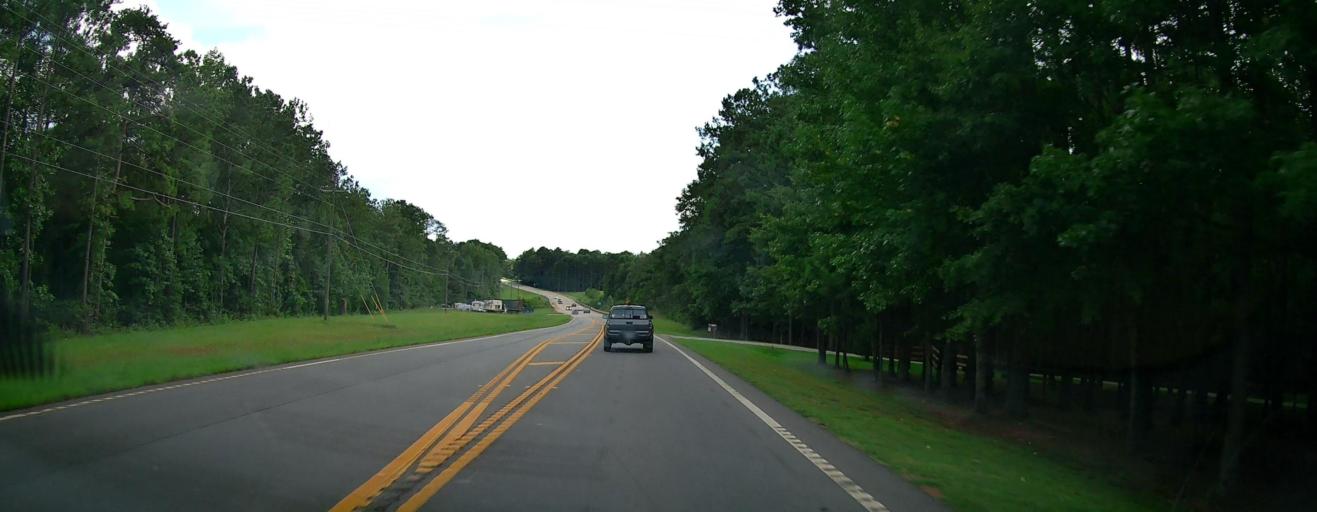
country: US
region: Georgia
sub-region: Harris County
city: Hamilton
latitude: 32.7113
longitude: -84.8716
